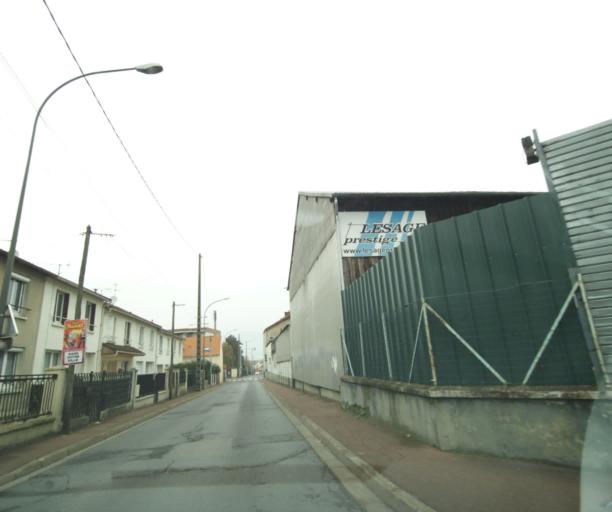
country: FR
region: Ile-de-France
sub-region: Departement de Seine-Saint-Denis
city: Vaujours
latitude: 48.9349
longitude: 2.5748
